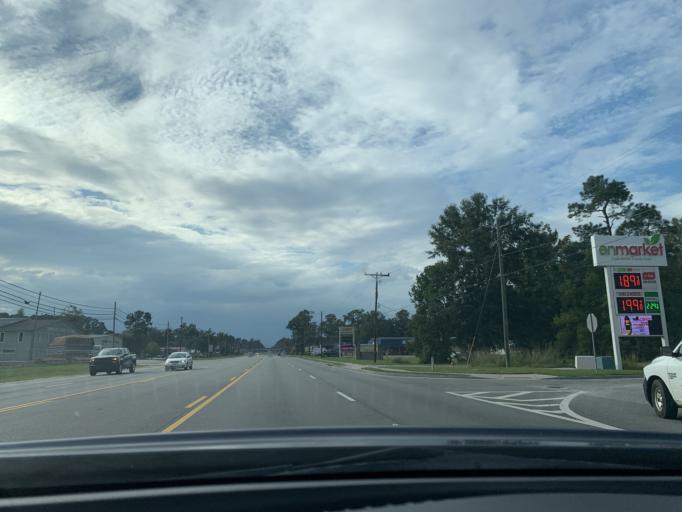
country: US
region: Georgia
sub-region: Chatham County
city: Pooler
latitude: 32.1200
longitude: -81.2599
